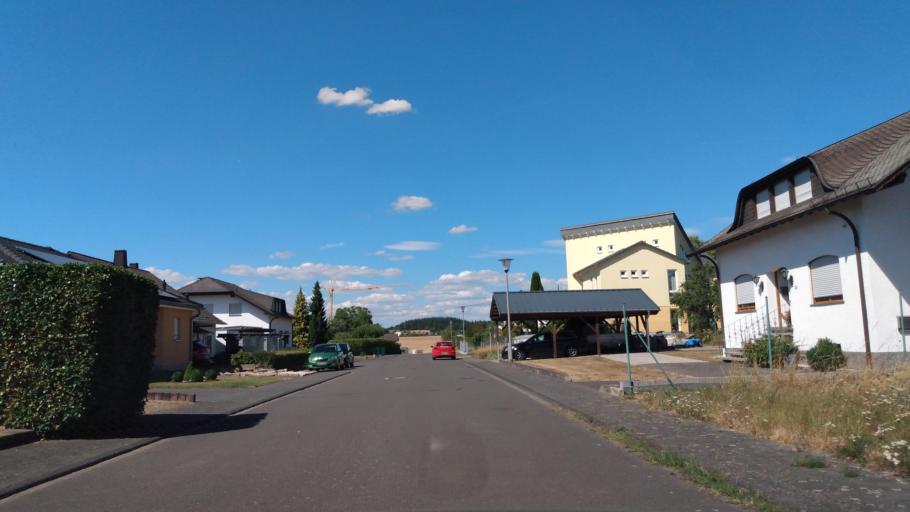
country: DE
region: Rheinland-Pfalz
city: Hupperath
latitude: 49.9985
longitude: 6.8406
